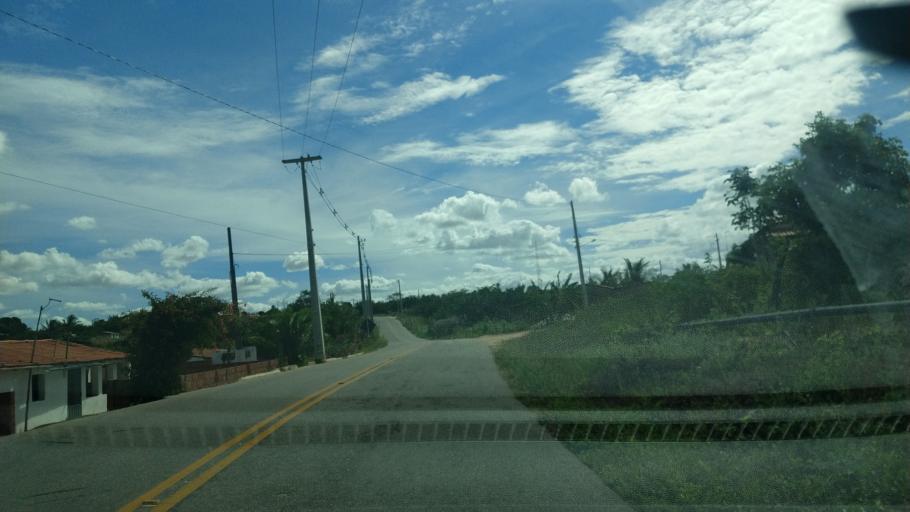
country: BR
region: Rio Grande do Norte
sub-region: Sao Jose Do Campestre
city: Sao Jose do Campestre
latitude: -6.4229
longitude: -35.7318
